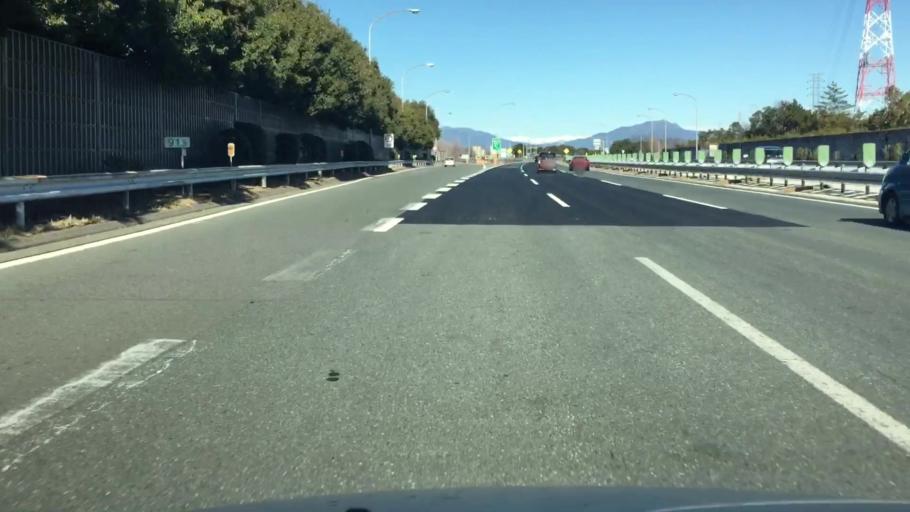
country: JP
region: Gunma
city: Maebashi-shi
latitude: 36.3714
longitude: 139.0288
